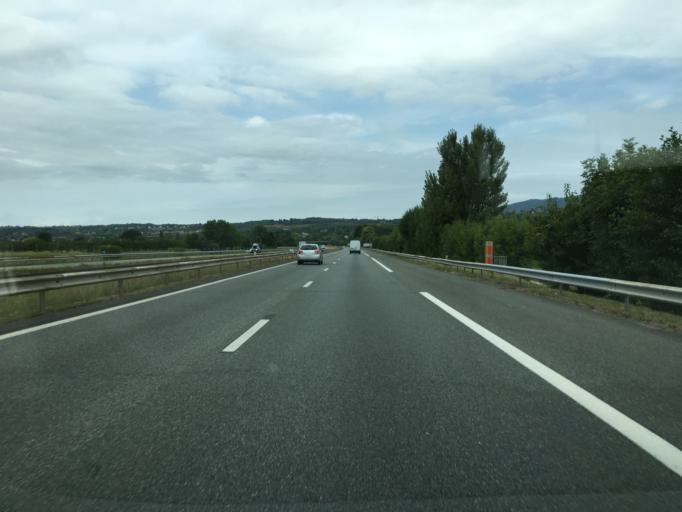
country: FR
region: Rhone-Alpes
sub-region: Departement de l'Isere
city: Saint-Jean-de-Moirans
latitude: 45.3300
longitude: 5.5921
